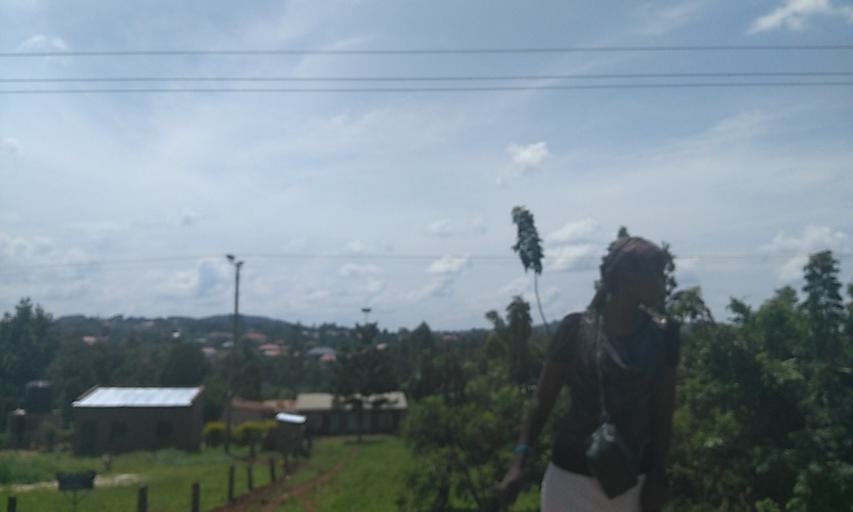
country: UG
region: Central Region
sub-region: Wakiso District
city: Wakiso
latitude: 0.4103
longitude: 32.4630
